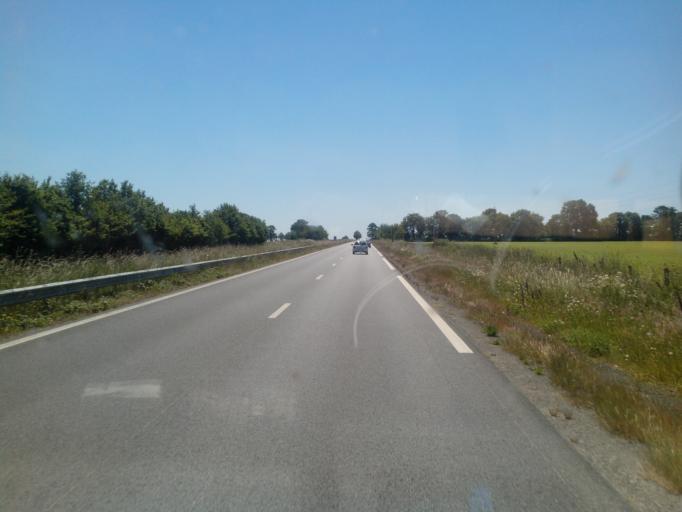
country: FR
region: Brittany
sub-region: Departement d'Ille-et-Vilaine
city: Chevaigne
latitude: 48.2217
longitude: -1.6233
